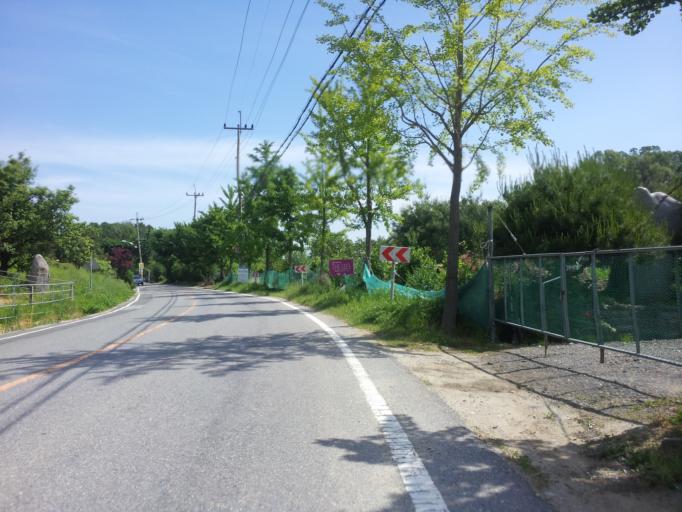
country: KR
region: Daejeon
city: Daejeon
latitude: 36.3394
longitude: 127.4784
